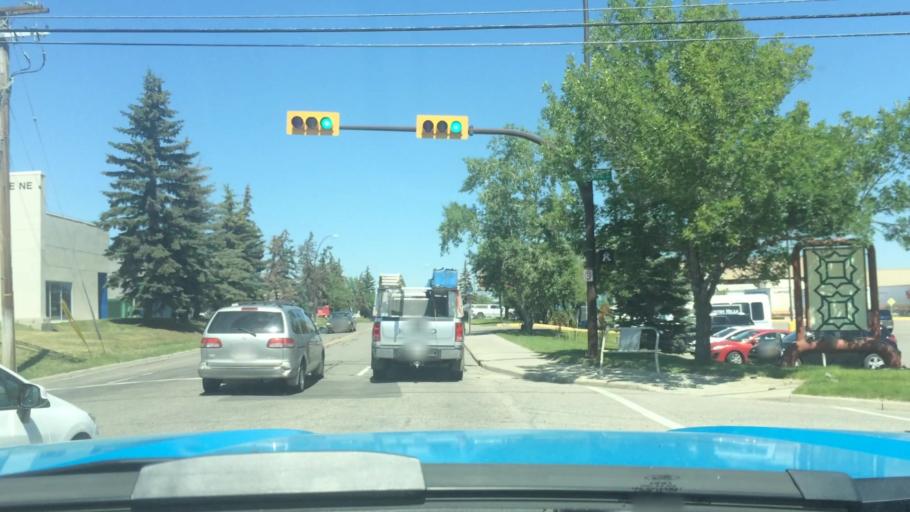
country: CA
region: Alberta
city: Calgary
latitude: 51.0523
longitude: -113.9932
